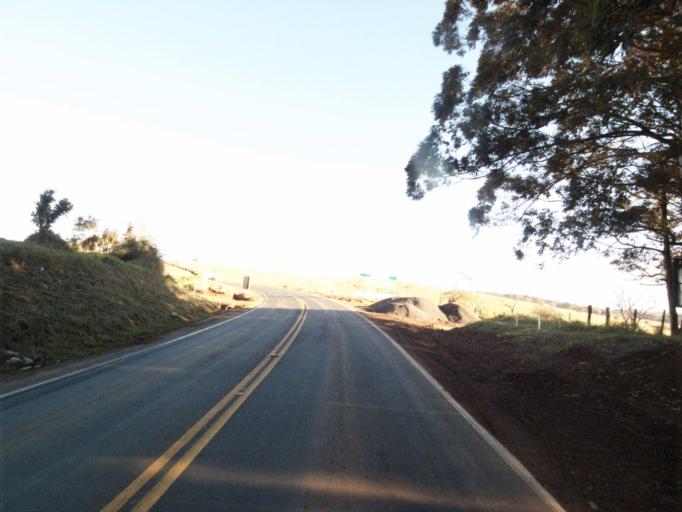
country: AR
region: Misiones
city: Bernardo de Irigoyen
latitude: -26.2881
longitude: -53.5558
